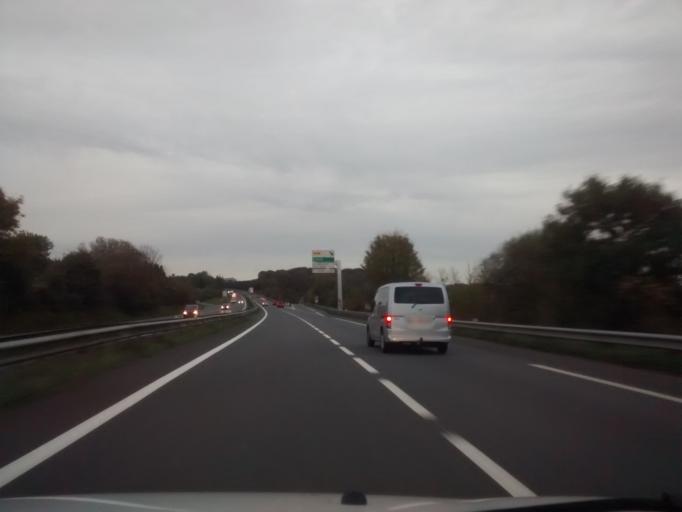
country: FR
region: Brittany
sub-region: Departement d'Ille-et-Vilaine
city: Quedillac
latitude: 48.2671
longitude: -2.1495
